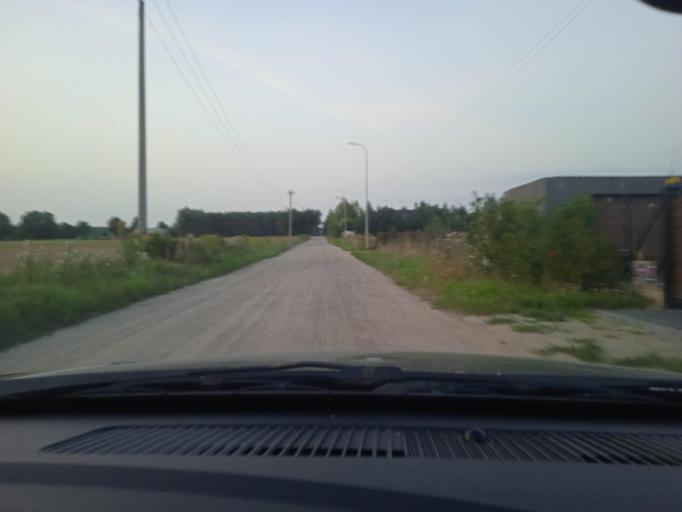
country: PL
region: Masovian Voivodeship
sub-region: Powiat nowodworski
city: Pomiechowek
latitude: 52.4862
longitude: 20.7025
